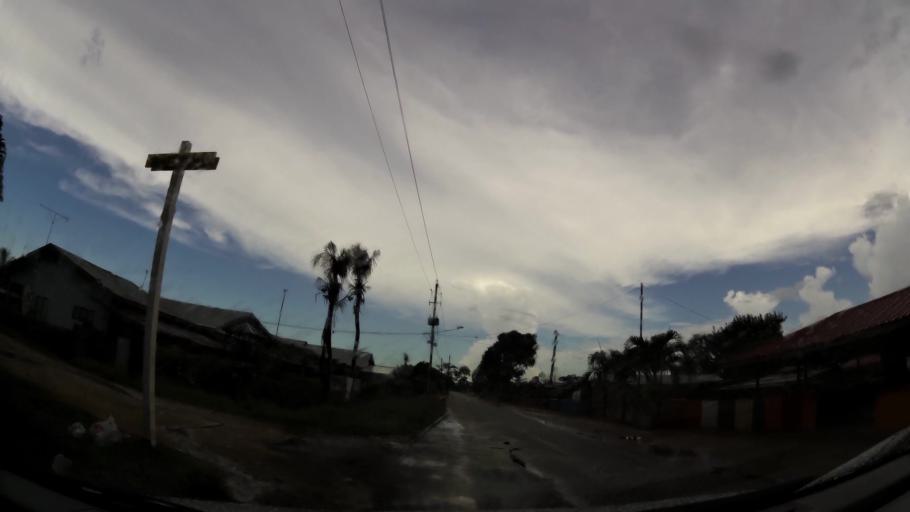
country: SR
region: Commewijne
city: Nieuw Amsterdam
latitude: 5.8853
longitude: -55.0586
